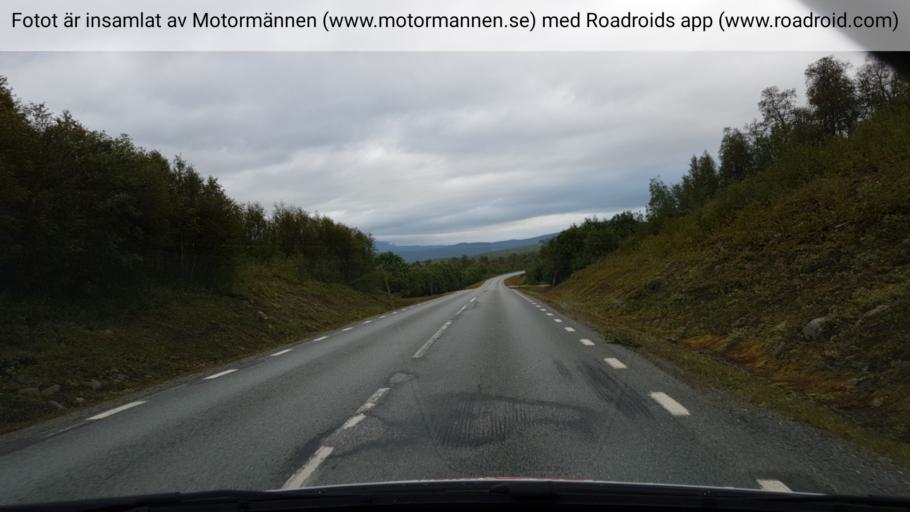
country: NO
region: Nordland
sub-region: Rana
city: Mo i Rana
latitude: 65.9634
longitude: 15.0379
